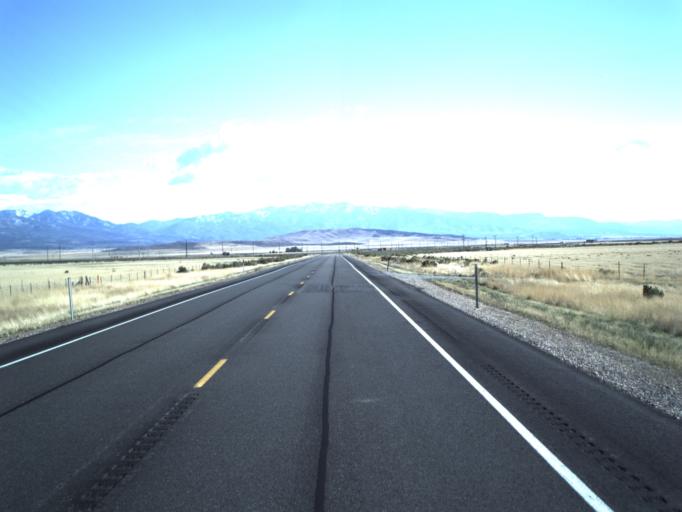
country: US
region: Utah
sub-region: Millard County
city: Fillmore
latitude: 39.1270
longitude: -112.3592
